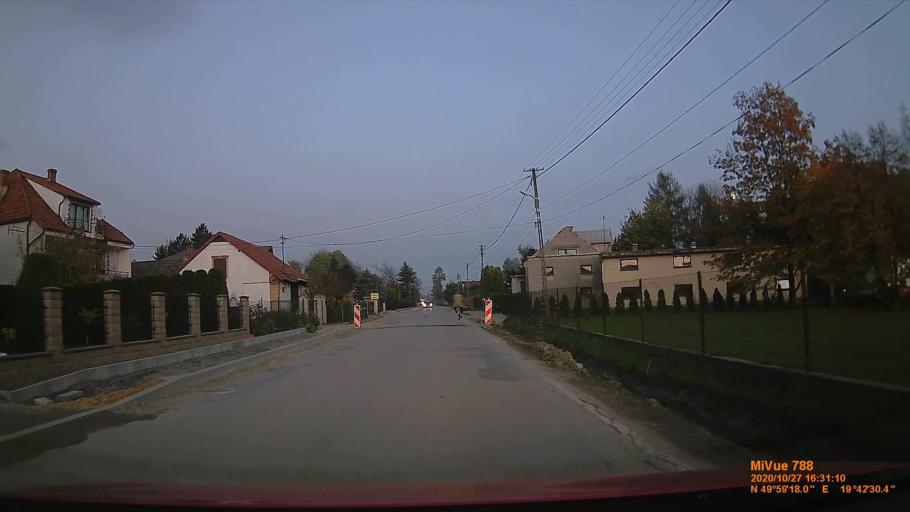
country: PL
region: Lesser Poland Voivodeship
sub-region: Powiat krakowski
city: Wolowice
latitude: 49.9883
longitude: 19.7086
